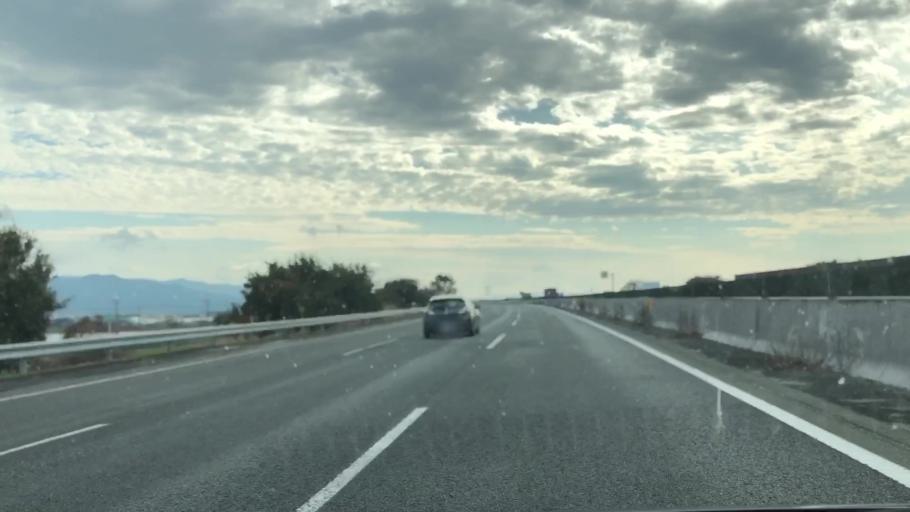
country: JP
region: Saga Prefecture
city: Tosu
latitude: 33.3501
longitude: 130.5376
